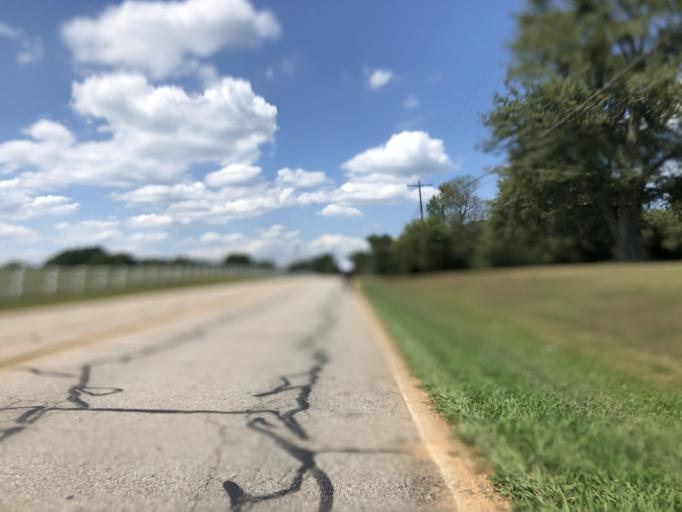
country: US
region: Georgia
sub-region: Fulton County
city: Palmetto
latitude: 33.5255
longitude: -84.6833
